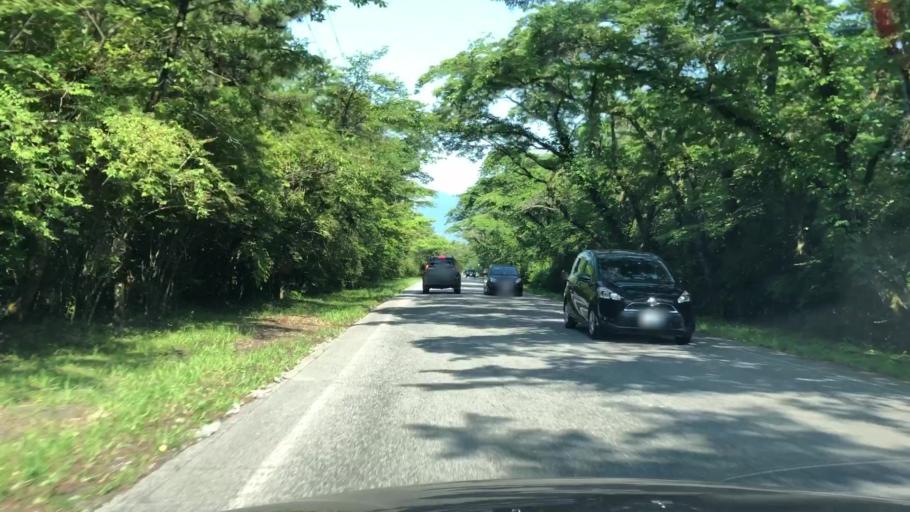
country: JP
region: Shizuoka
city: Gotemba
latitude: 35.3257
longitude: 138.8603
